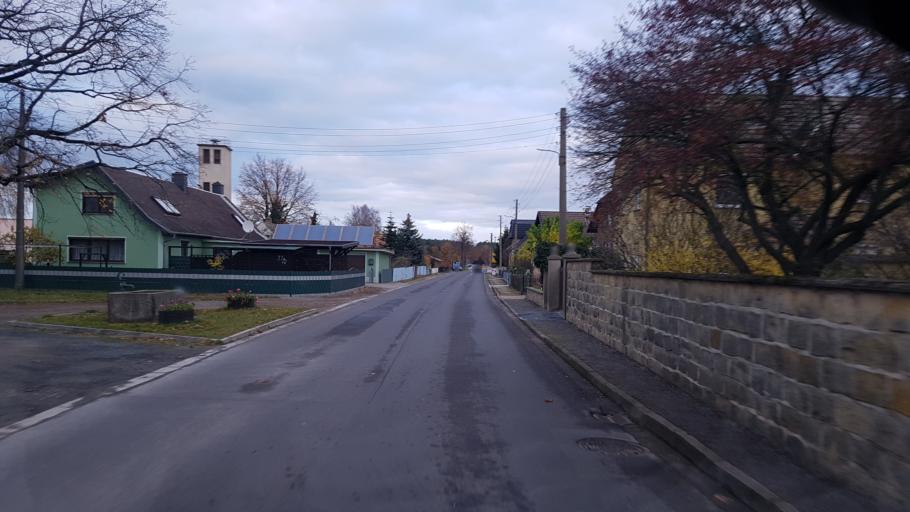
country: DE
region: Brandenburg
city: Ortrand
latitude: 51.3808
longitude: 13.7588
